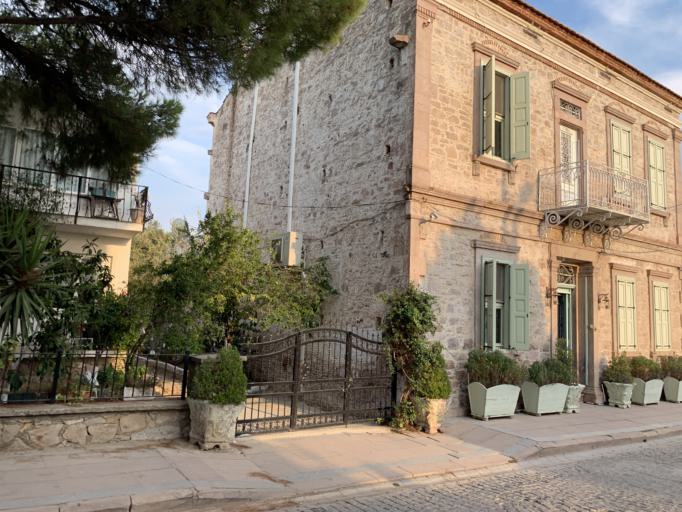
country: TR
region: Balikesir
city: Ayvalik
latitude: 39.3339
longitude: 26.6557
